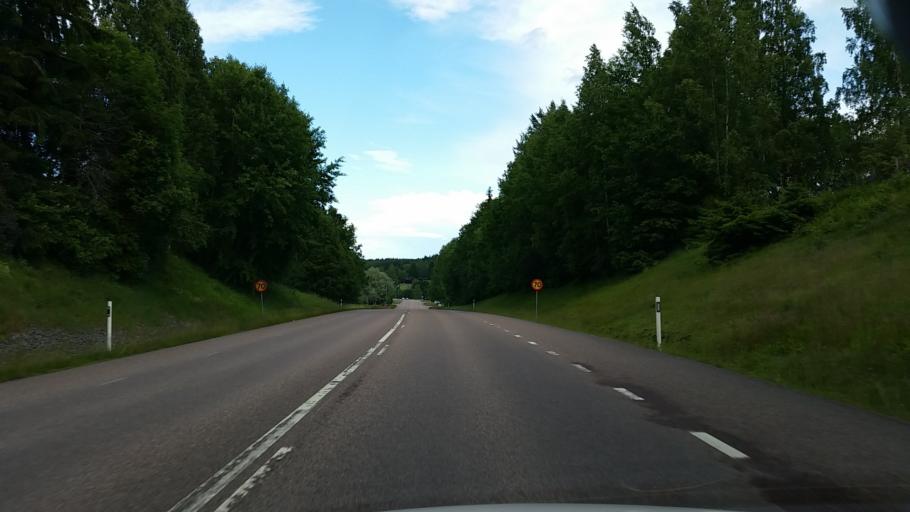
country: SE
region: Dalarna
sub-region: Smedjebackens Kommun
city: Smedjebacken
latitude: 60.1398
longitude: 15.3051
